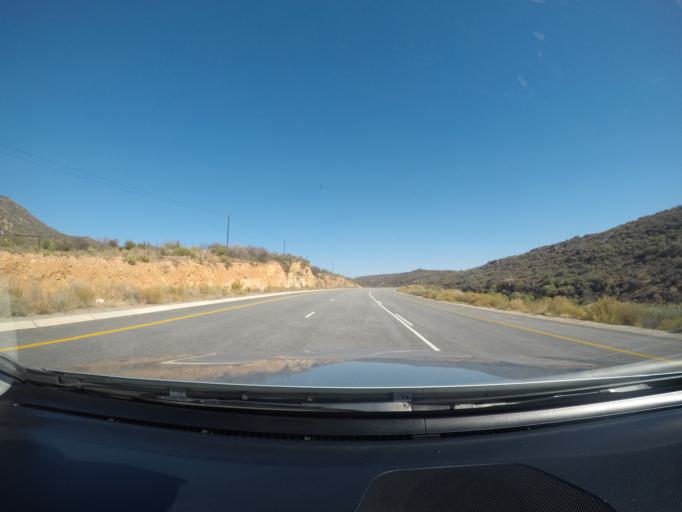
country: ZA
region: Western Cape
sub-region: West Coast District Municipality
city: Clanwilliam
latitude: -32.3417
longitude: 18.9252
